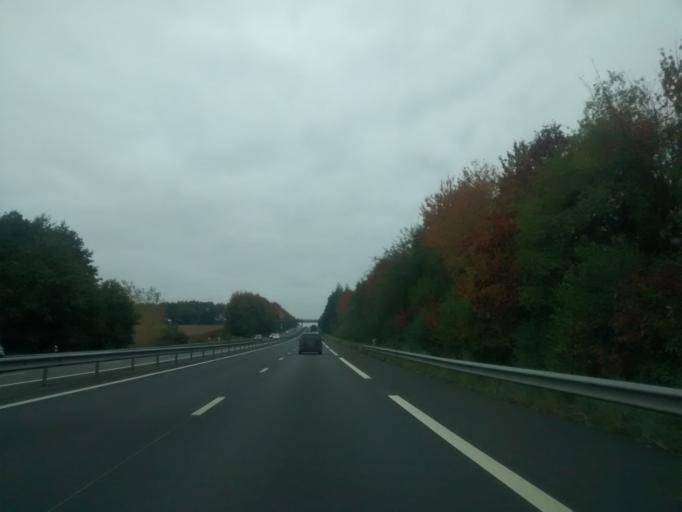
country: FR
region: Brittany
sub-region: Departement d'Ille-et-Vilaine
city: Tinteniac
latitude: 48.3140
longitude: -1.8409
